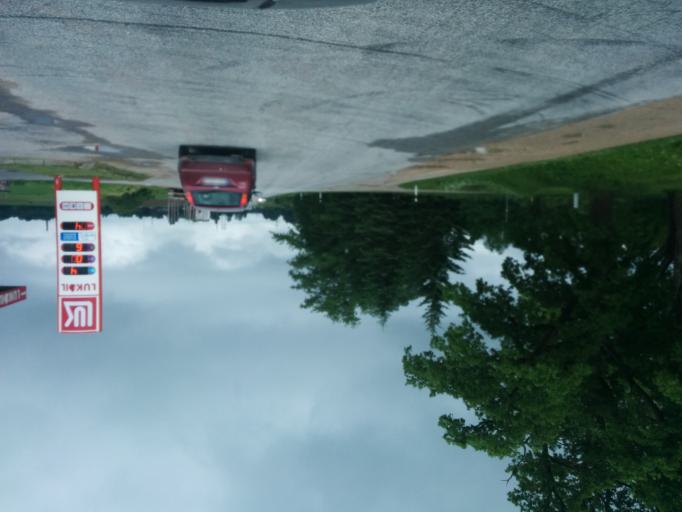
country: LV
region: Beverina
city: Murmuiza
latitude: 57.5081
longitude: 25.4608
